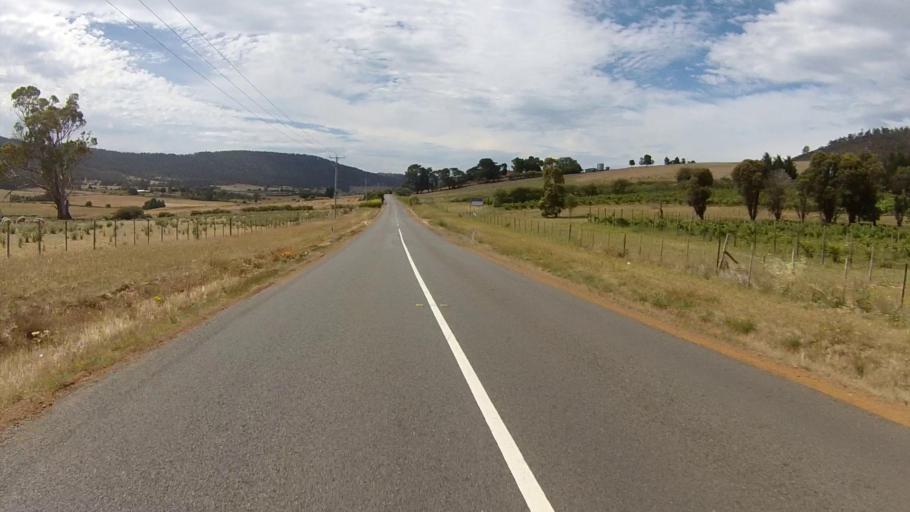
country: AU
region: Tasmania
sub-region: Brighton
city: Old Beach
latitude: -42.7003
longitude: 147.3588
